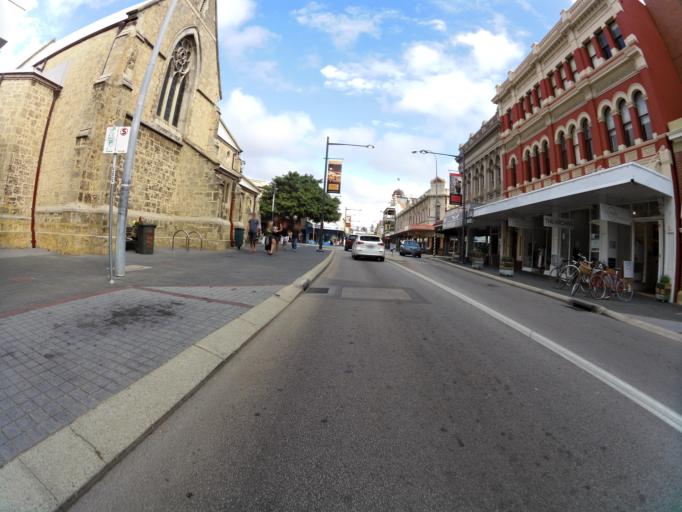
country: AU
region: Western Australia
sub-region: Fremantle
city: South Fremantle
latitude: -32.0537
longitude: 115.7461
